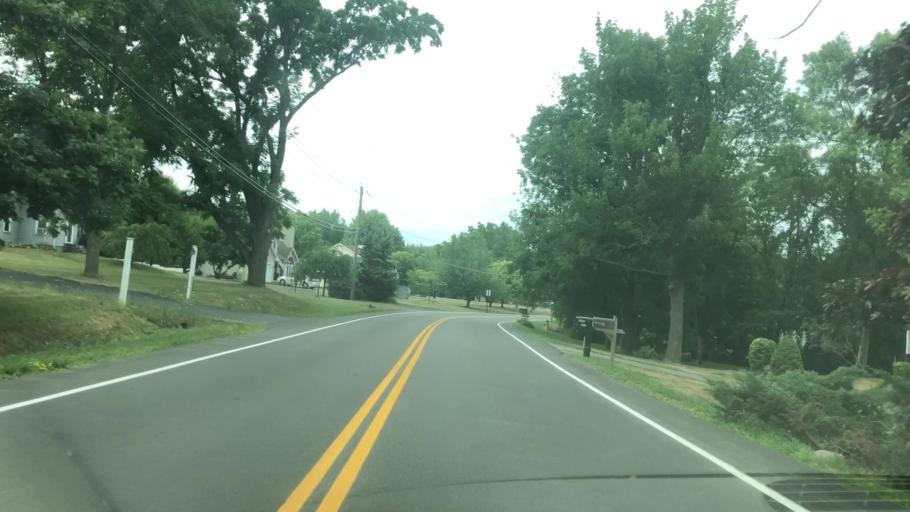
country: US
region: New York
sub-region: Wayne County
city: Macedon
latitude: 43.1305
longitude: -77.3534
